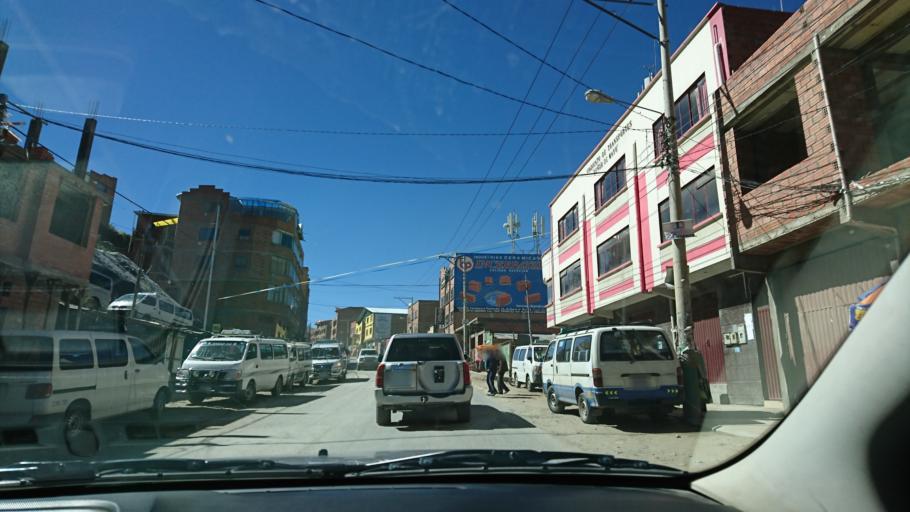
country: BO
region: La Paz
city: La Paz
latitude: -16.4516
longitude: -68.0920
